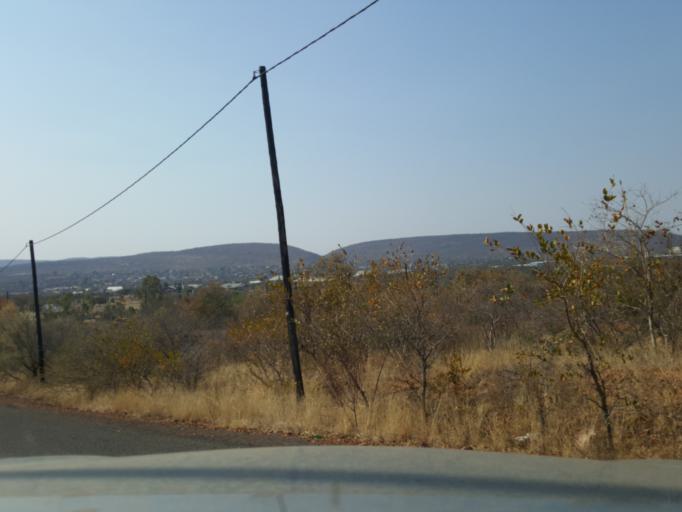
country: BW
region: South East
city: Lobatse
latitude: -25.1802
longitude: 25.6799
